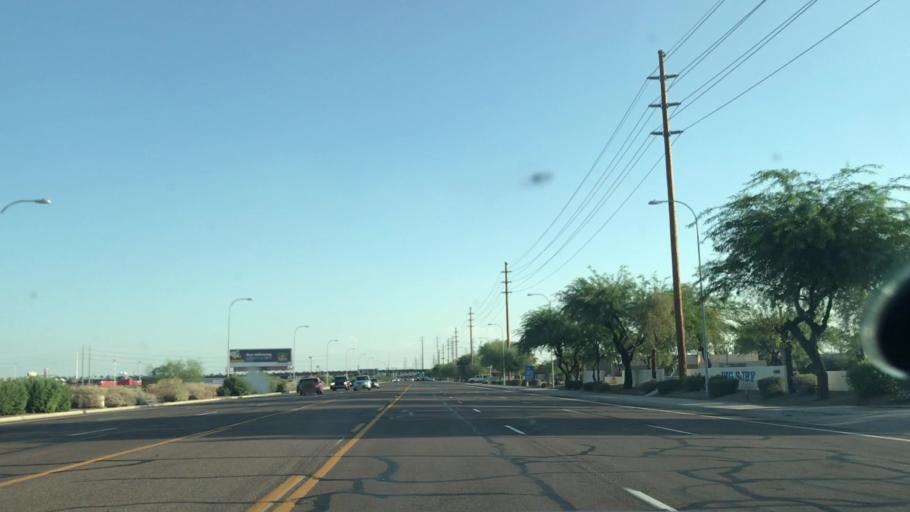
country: US
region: Arizona
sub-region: Maricopa County
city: Tempe
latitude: 33.4458
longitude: -111.9095
